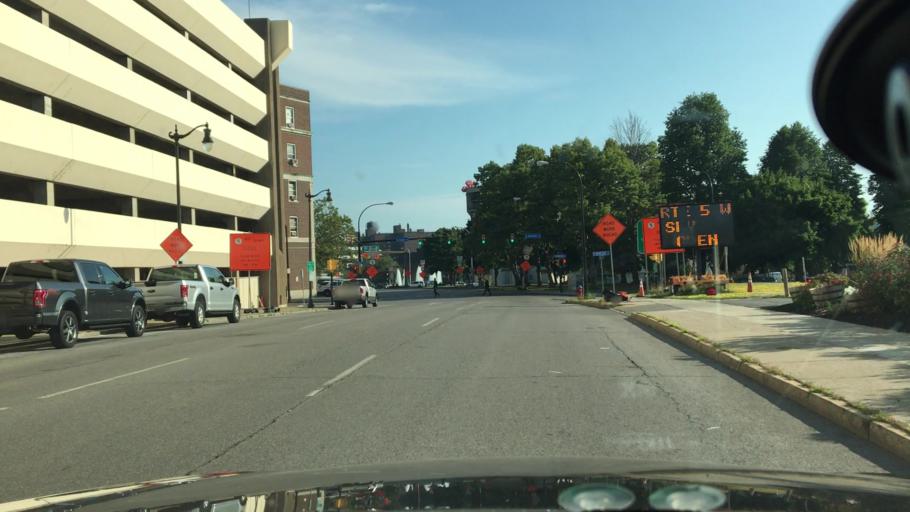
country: US
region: New York
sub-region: Erie County
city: Buffalo
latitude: 42.8859
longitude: -78.8801
